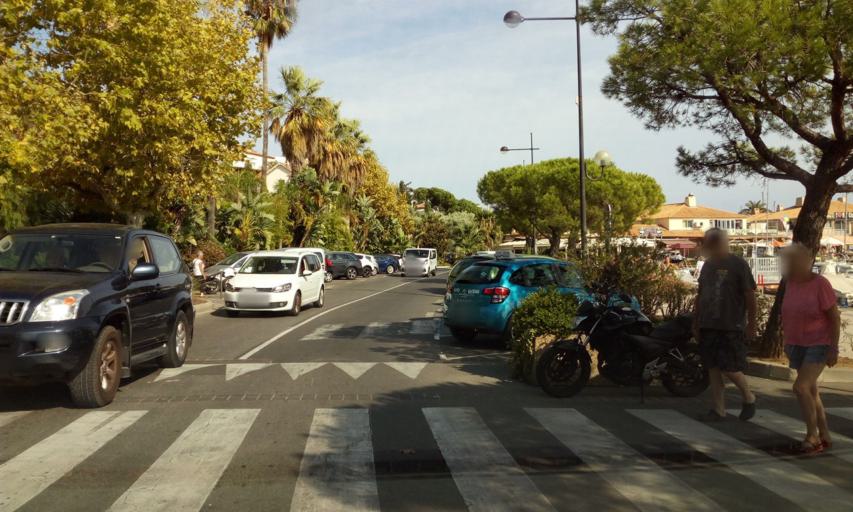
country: FR
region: Provence-Alpes-Cote d'Azur
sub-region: Departement du Var
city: Le Lavandou
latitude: 43.1380
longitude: 6.3726
